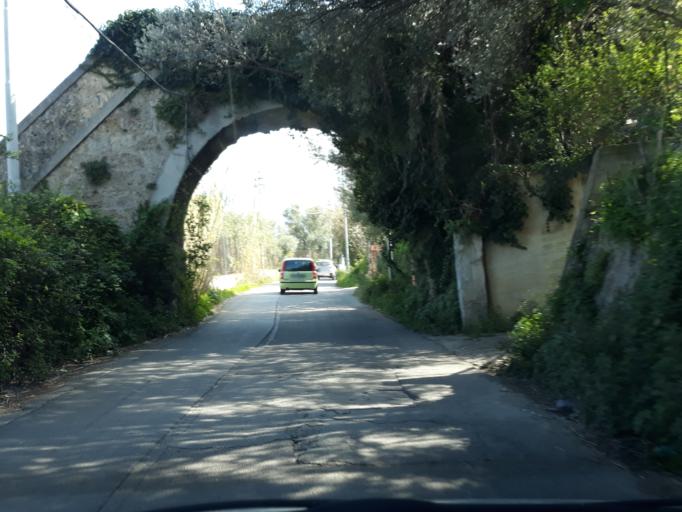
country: IT
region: Sicily
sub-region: Palermo
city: Monreale
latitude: 38.0725
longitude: 13.2830
